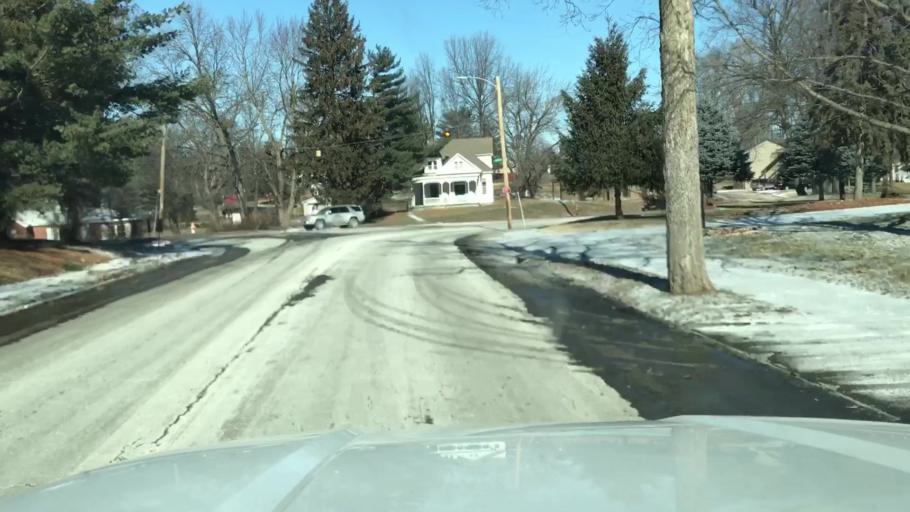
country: US
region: Missouri
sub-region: Andrew County
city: Country Club Village
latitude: 39.7975
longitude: -94.8195
